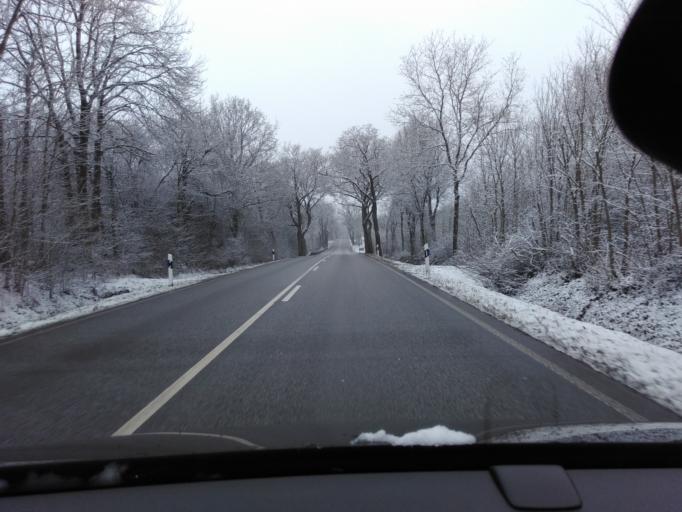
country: DE
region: Schleswig-Holstein
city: Ahrensbok
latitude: 54.0044
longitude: 10.5474
